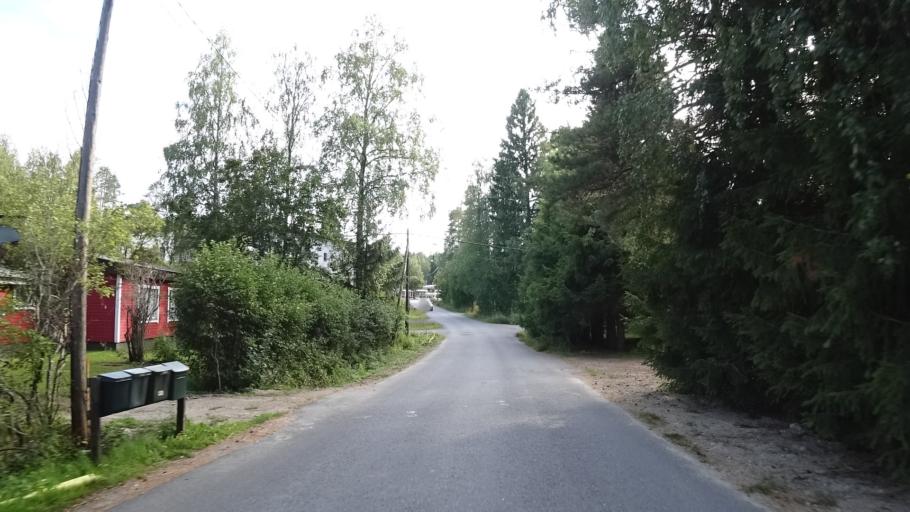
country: FI
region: North Karelia
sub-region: Joensuu
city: Eno
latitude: 62.8001
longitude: 30.1601
